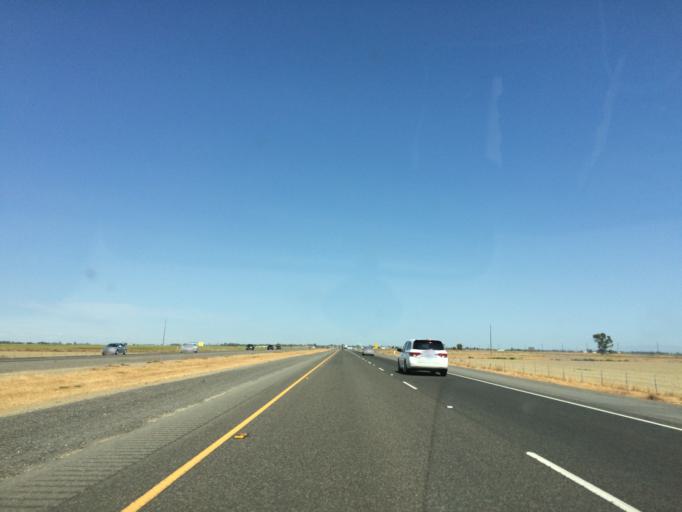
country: US
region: California
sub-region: Glenn County
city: Willows
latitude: 39.4705
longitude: -122.1958
